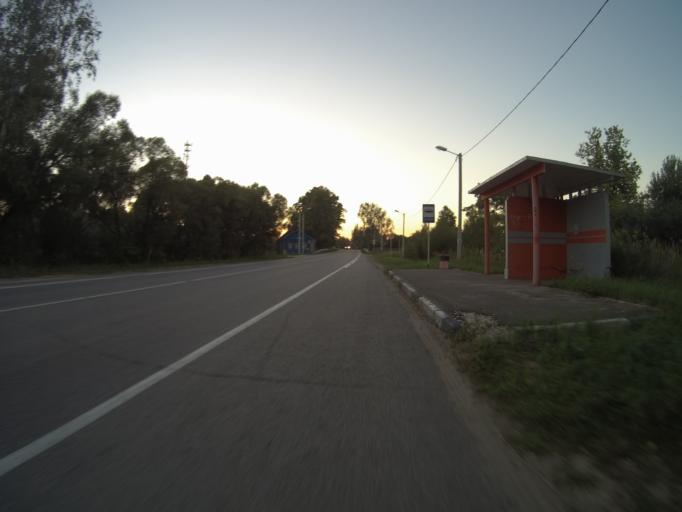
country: RU
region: Vladimir
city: Golovino
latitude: 55.9282
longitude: 40.5972
